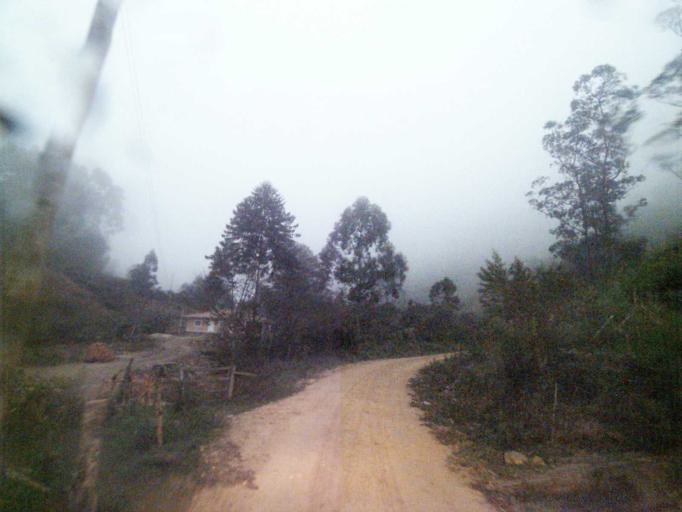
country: BR
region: Santa Catarina
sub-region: Anitapolis
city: Anitapolis
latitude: -27.7958
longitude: -49.1388
